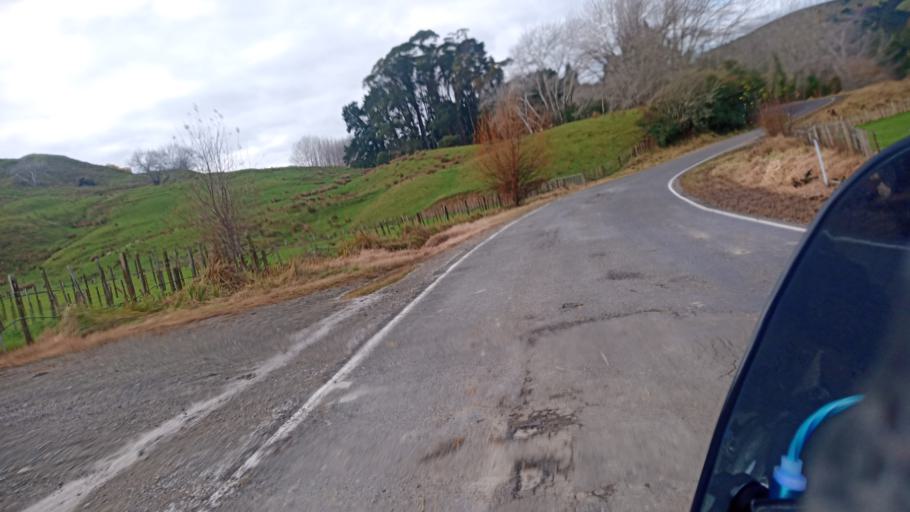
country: NZ
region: Gisborne
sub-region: Gisborne District
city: Gisborne
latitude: -38.4312
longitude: 177.9102
